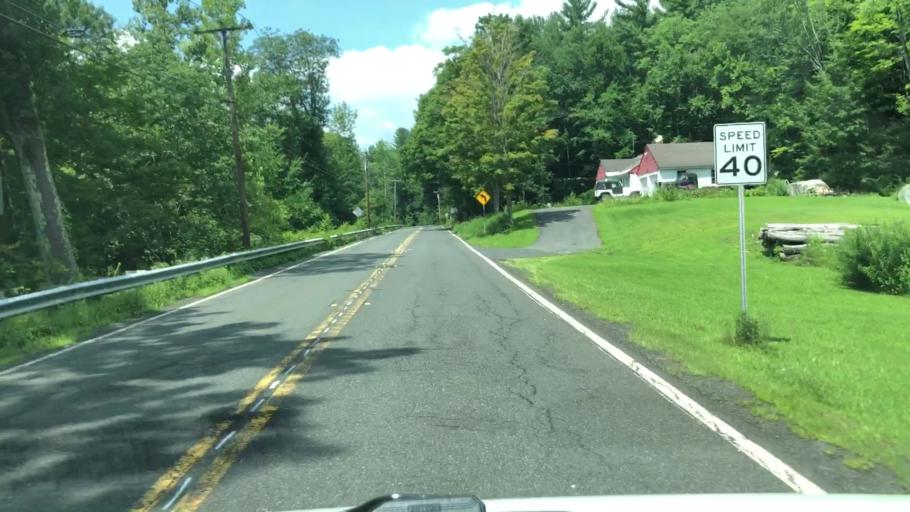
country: US
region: Massachusetts
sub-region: Franklin County
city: Ashfield
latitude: 42.5150
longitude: -72.7452
